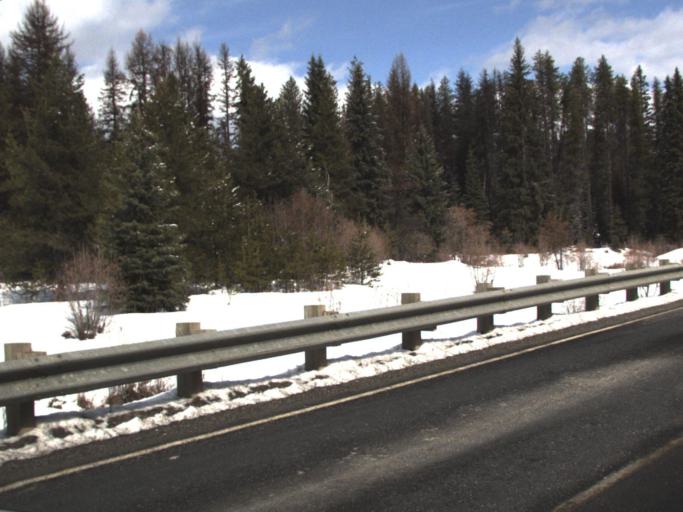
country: US
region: Washington
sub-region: Stevens County
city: Colville
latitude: 48.6662
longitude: -117.4754
